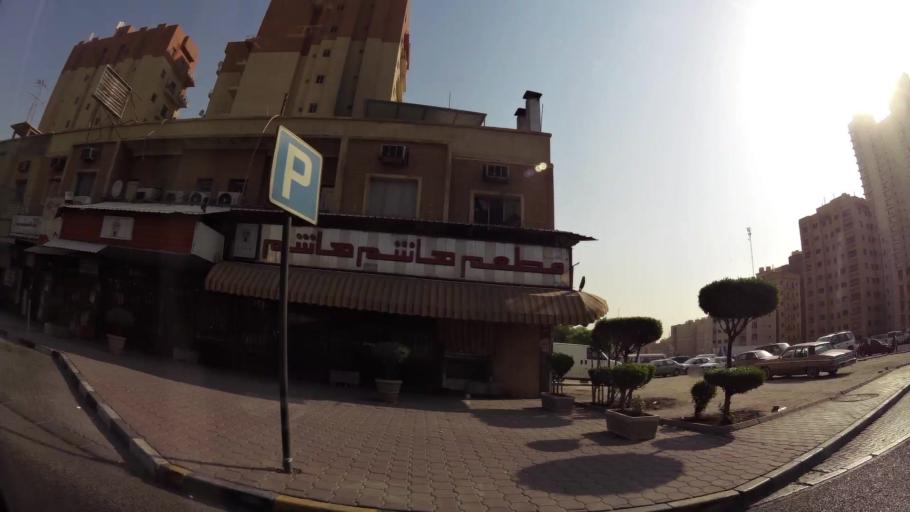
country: KW
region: Muhafazat Hawalli
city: Hawalli
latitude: 29.3320
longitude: 48.0273
